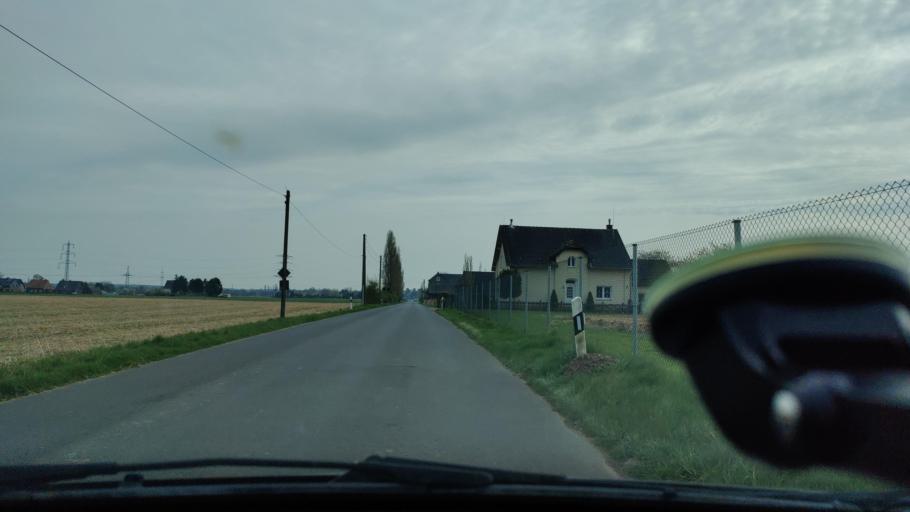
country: DE
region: North Rhine-Westphalia
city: Rheinberg
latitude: 51.5172
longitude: 6.6398
